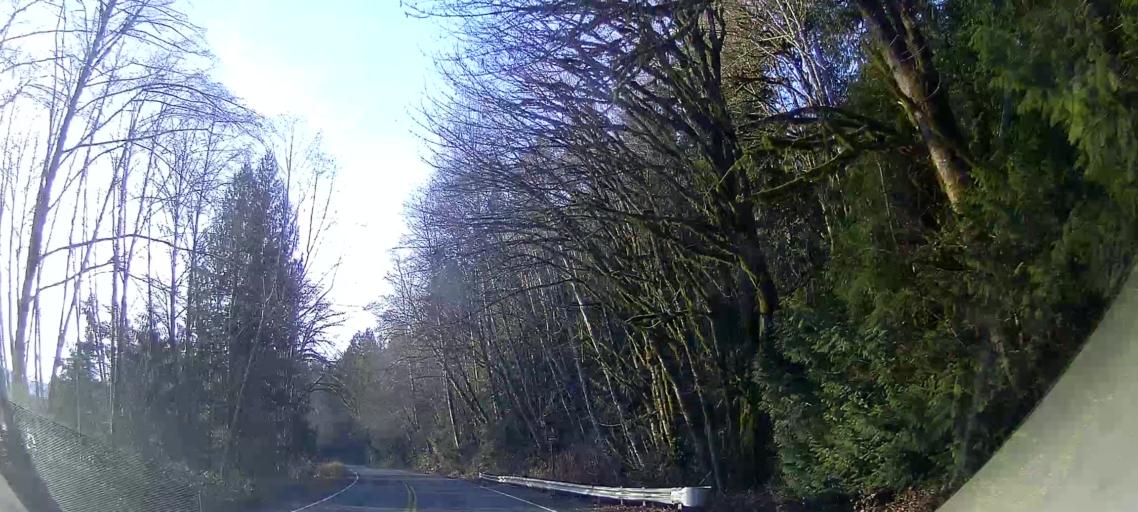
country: US
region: Washington
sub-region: Snohomish County
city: Darrington
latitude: 48.5674
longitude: -121.8008
